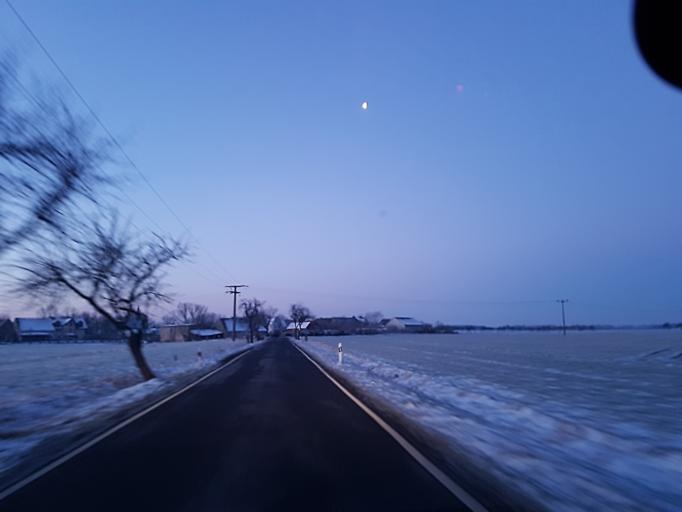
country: DE
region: Brandenburg
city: Muhlberg
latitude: 51.4631
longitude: 13.2591
